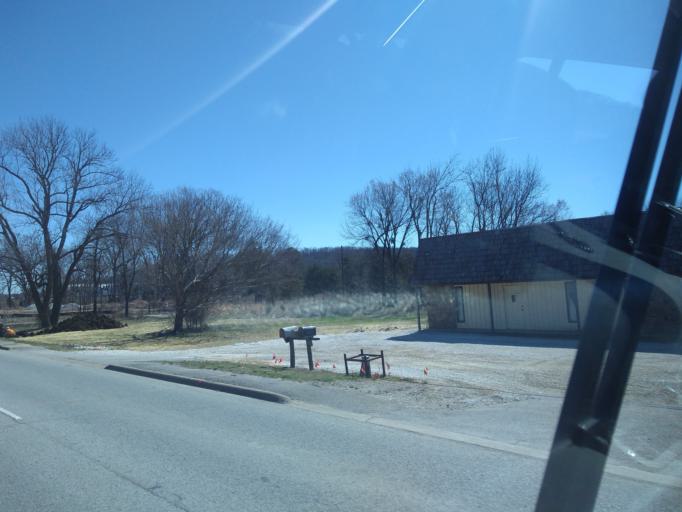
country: US
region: Arkansas
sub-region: Washington County
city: Farmington
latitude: 36.0499
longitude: -94.2111
